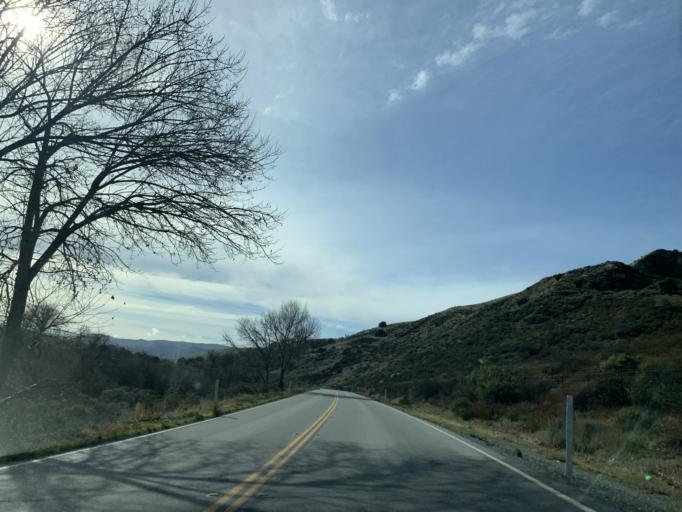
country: US
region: California
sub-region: San Benito County
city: Ridgemark
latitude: 36.7416
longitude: -121.2812
